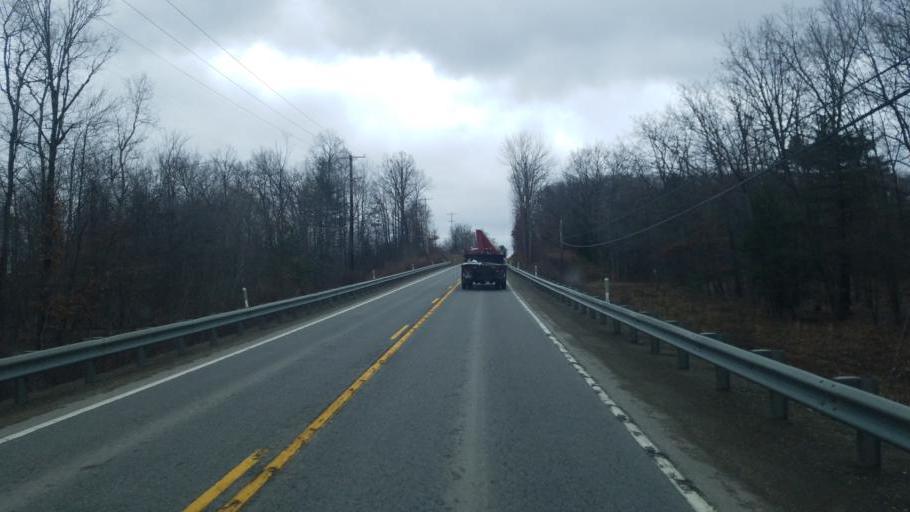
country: US
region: Pennsylvania
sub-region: Clarion County
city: Marianne
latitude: 41.3627
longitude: -79.3185
